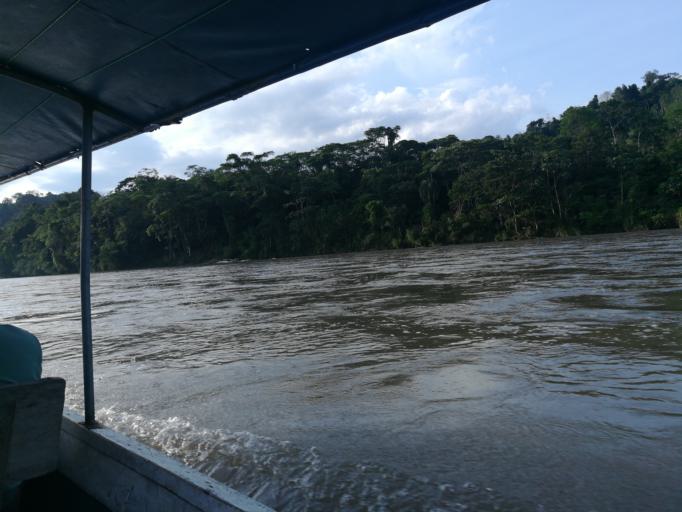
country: EC
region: Orellana
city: Boca Suno
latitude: -0.8798
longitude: -77.2903
